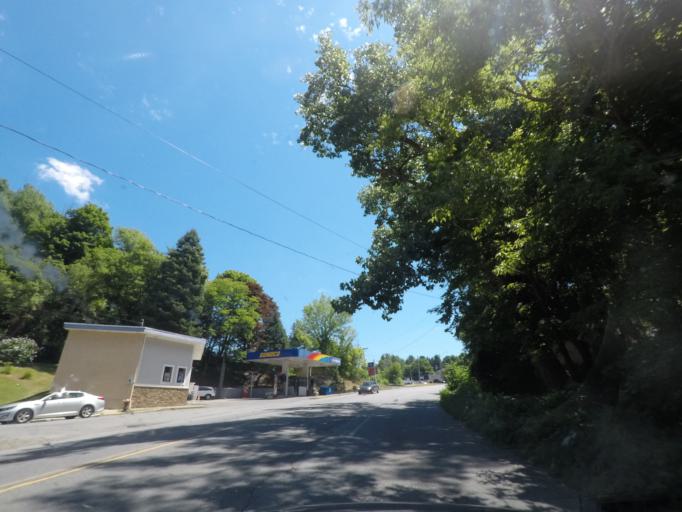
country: US
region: New York
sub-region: Rensselaer County
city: Troy
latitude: 42.7046
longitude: -73.6898
